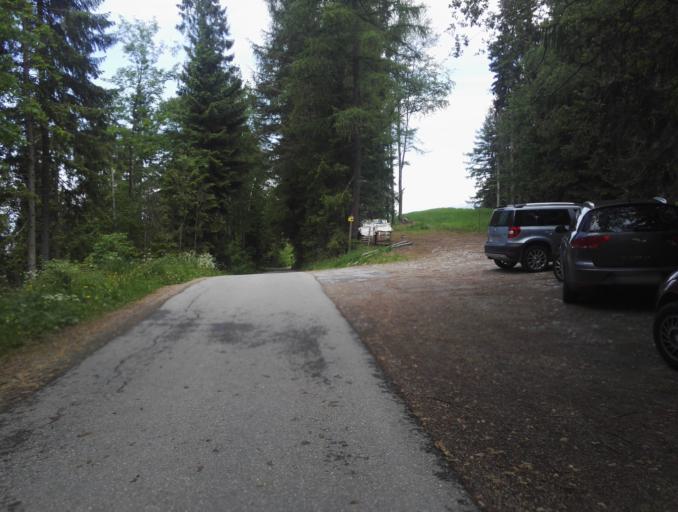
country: AT
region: Styria
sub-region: Politischer Bezirk Graz-Umgebung
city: Sankt Radegund bei Graz
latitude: 47.2071
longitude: 15.4588
